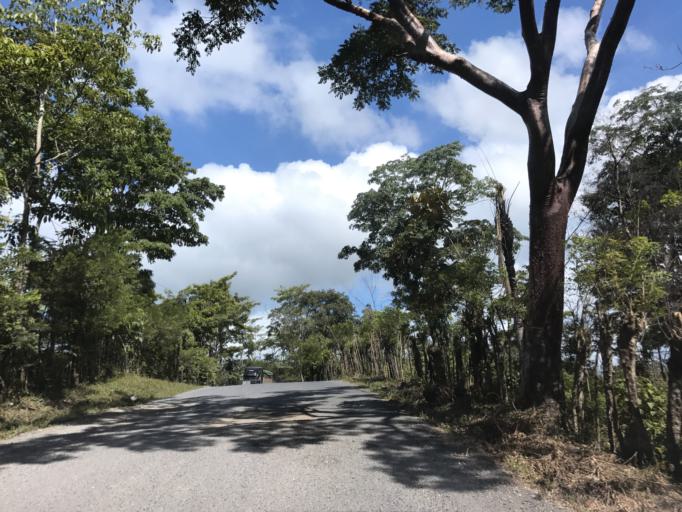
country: GT
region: Izabal
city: Morales
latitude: 15.6392
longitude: -89.0326
